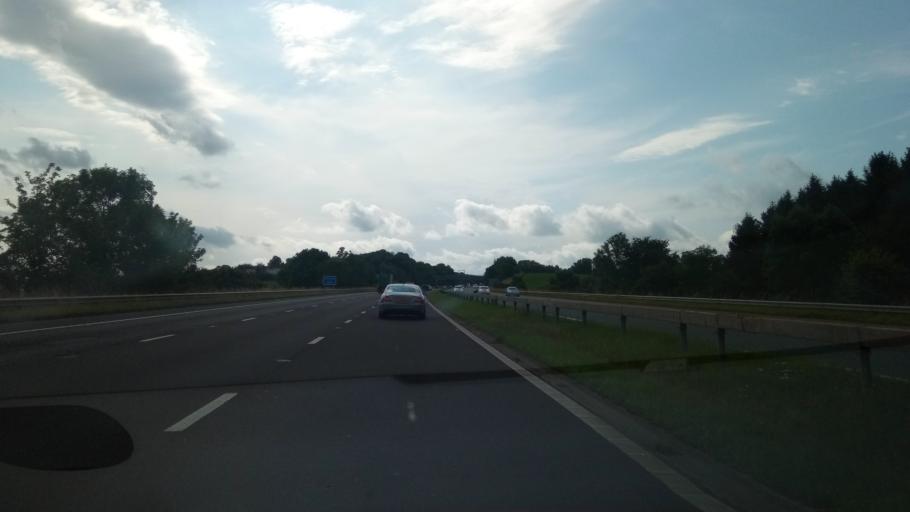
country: GB
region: England
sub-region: Cumbria
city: Penrith
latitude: 54.6407
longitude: -2.7340
